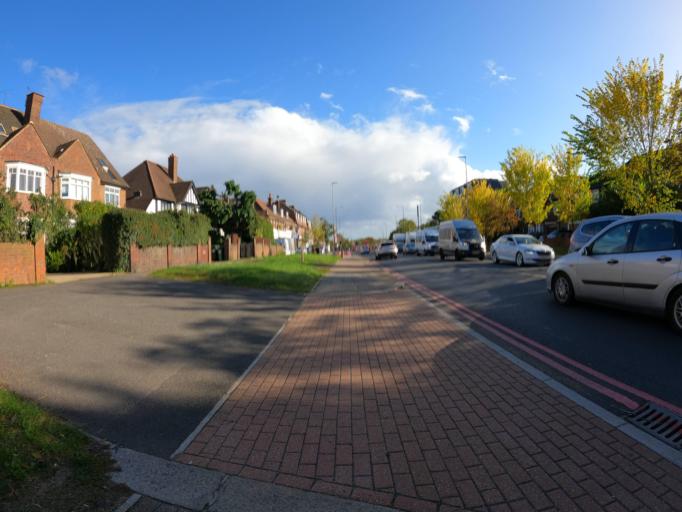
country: GB
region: England
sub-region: Greater London
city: Acton
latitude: 51.5019
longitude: -0.2864
